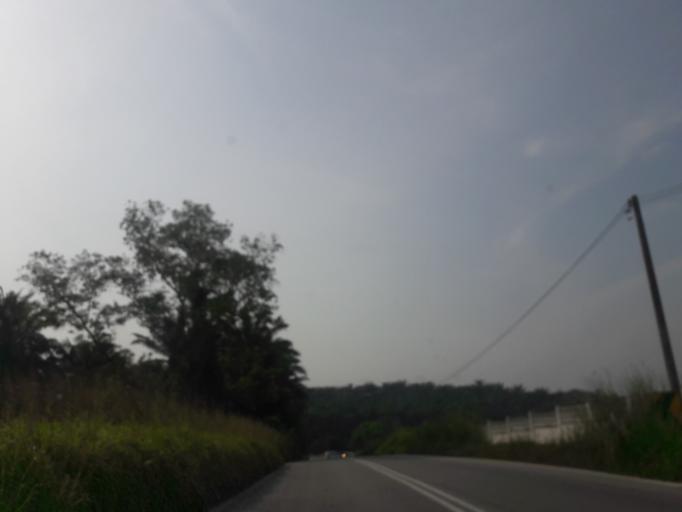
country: MY
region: Kedah
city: Kulim
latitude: 5.3707
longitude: 100.5213
